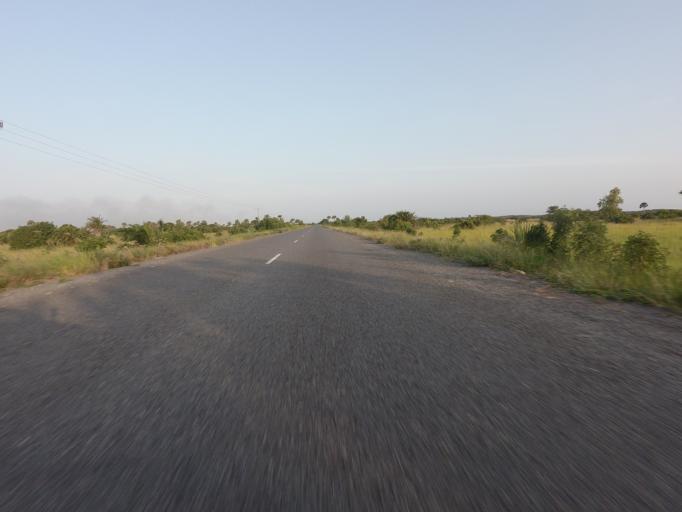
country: GH
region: Volta
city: Anloga
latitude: 5.8404
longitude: 0.7838
